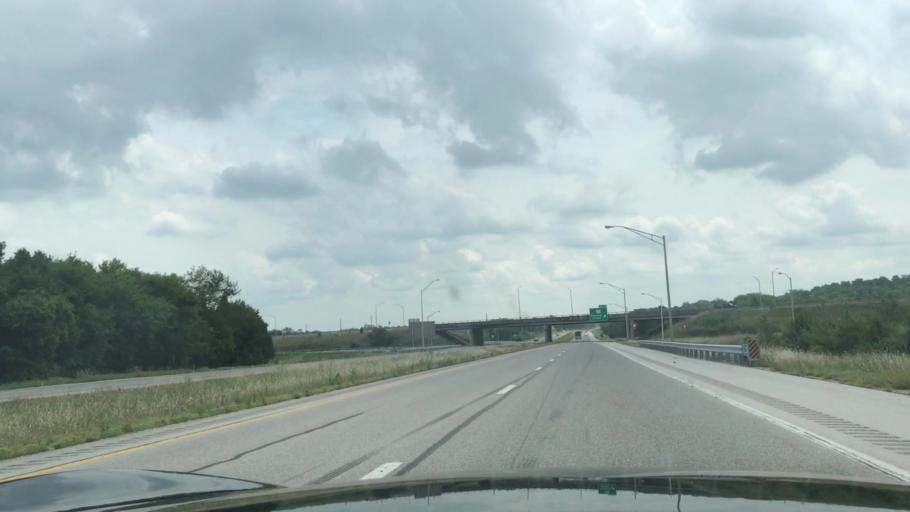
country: US
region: Kentucky
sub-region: Warren County
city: Bowling Green
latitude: 36.9945
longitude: -86.5048
